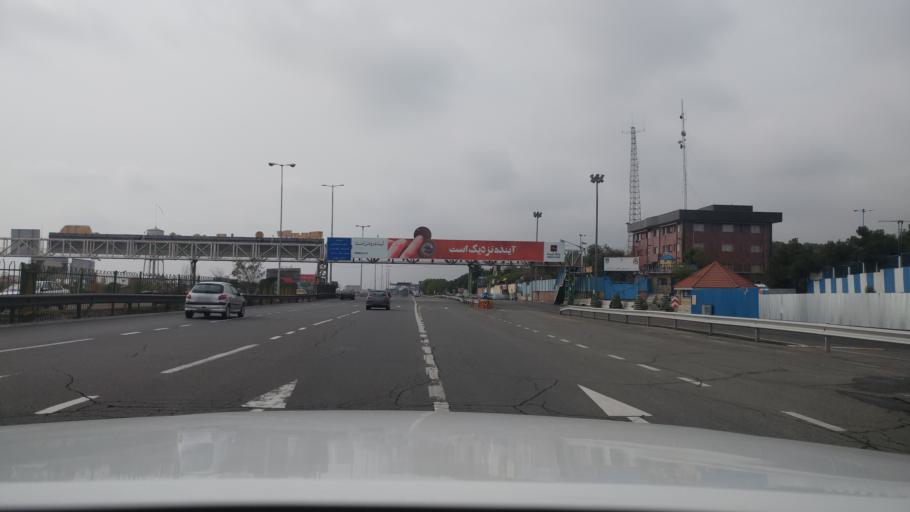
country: IR
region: Tehran
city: Shahr-e Qods
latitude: 35.7164
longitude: 51.2396
